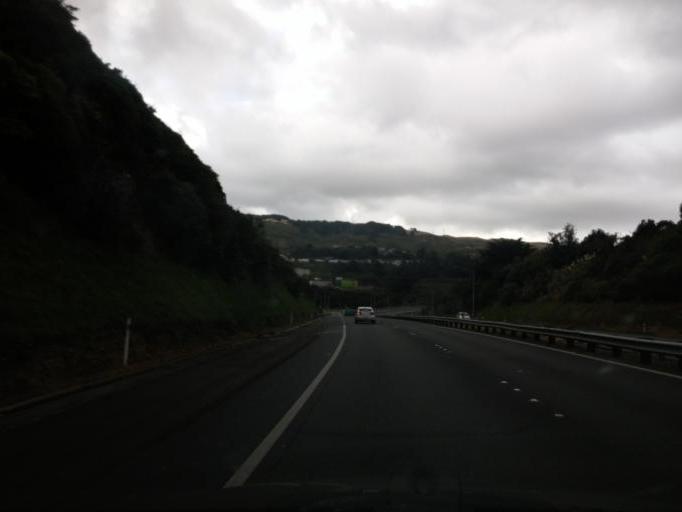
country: NZ
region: Wellington
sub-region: Porirua City
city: Porirua
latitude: -41.1821
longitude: 174.8295
